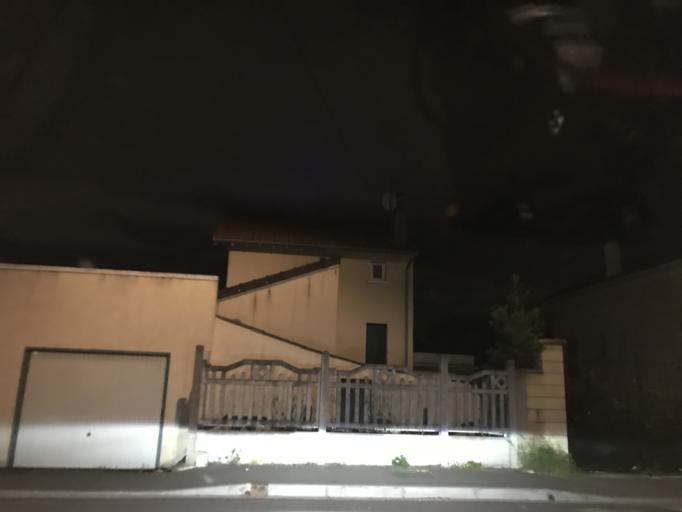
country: FR
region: Ile-de-France
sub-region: Departement du Val-d'Oise
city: Bezons
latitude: 48.9296
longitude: 2.2031
